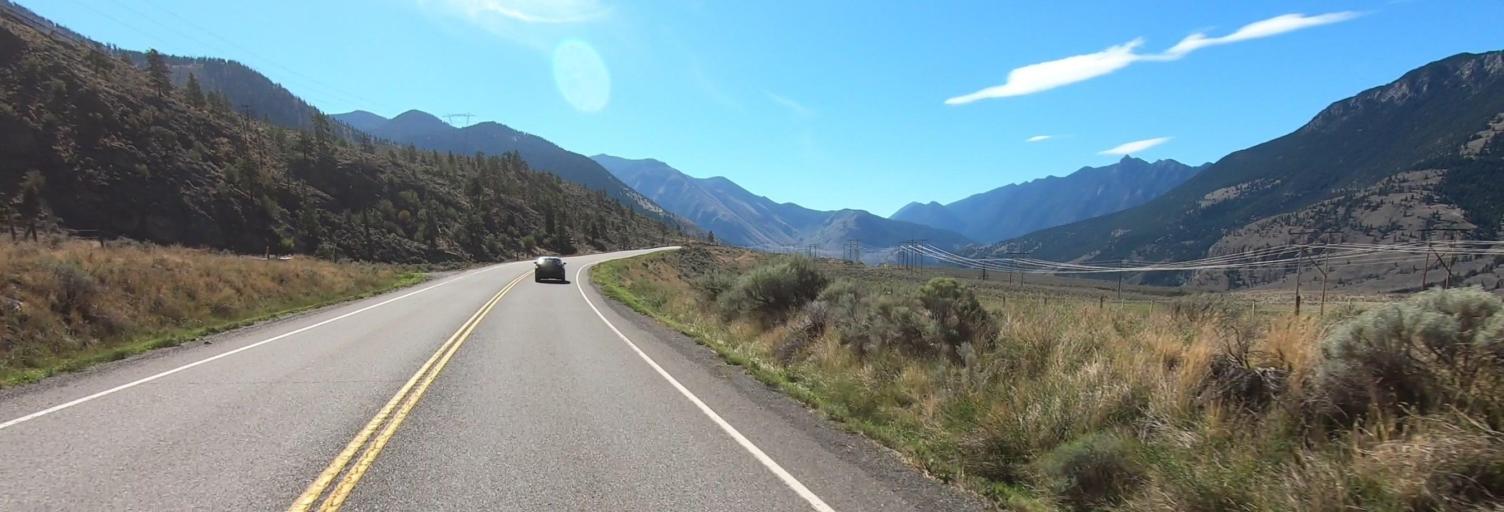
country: CA
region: British Columbia
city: Lillooet
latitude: 50.8169
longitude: -121.8525
